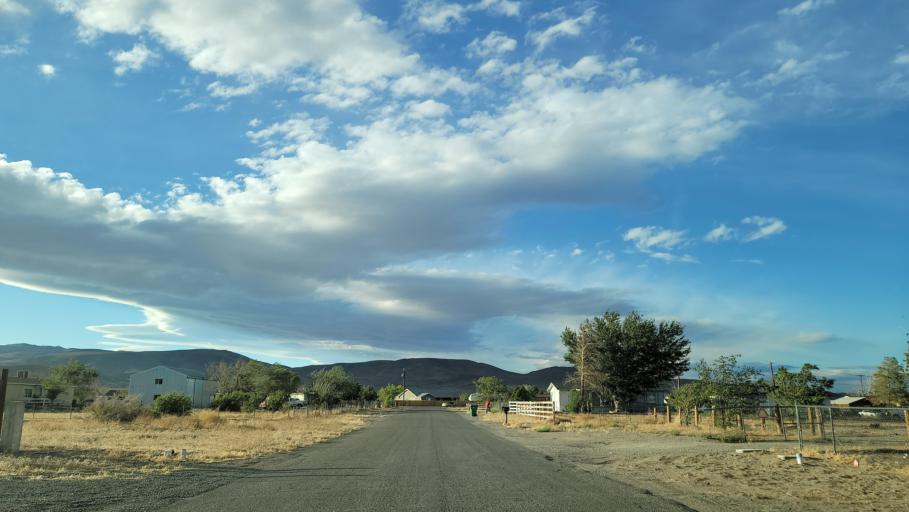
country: US
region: Nevada
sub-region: Lyon County
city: Silver Springs
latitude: 39.3989
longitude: -119.2374
